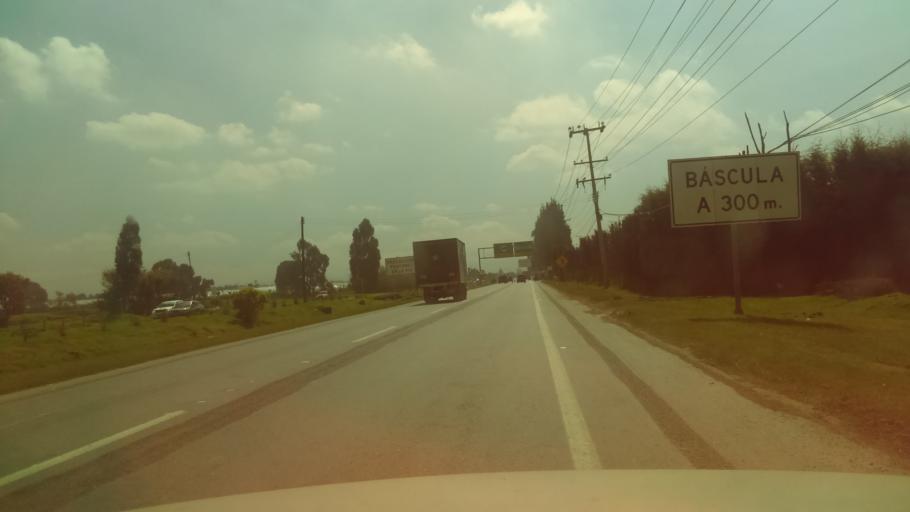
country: CO
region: Cundinamarca
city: Bojaca
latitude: 4.7555
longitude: -74.3030
